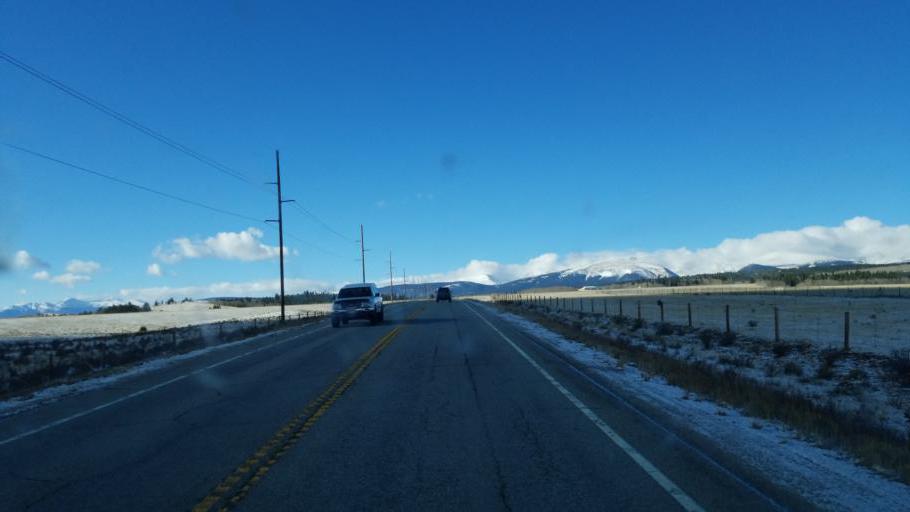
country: US
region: Colorado
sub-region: Park County
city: Fairplay
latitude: 39.2449
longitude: -105.9696
